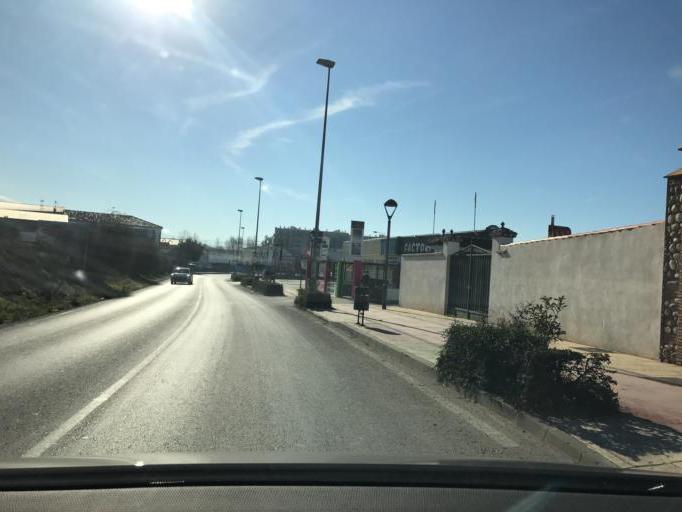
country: ES
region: Andalusia
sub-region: Provincia de Granada
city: Pulianas
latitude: 37.2155
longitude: -3.6095
